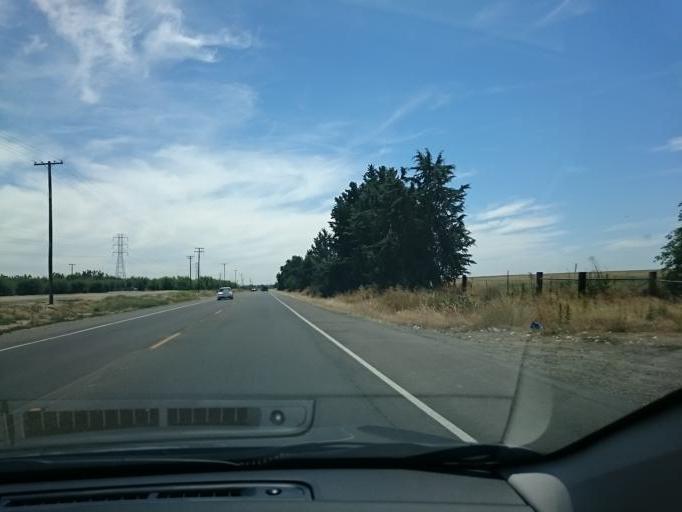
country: US
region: California
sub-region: Stanislaus County
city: Hughson
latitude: 37.6315
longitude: -120.8480
